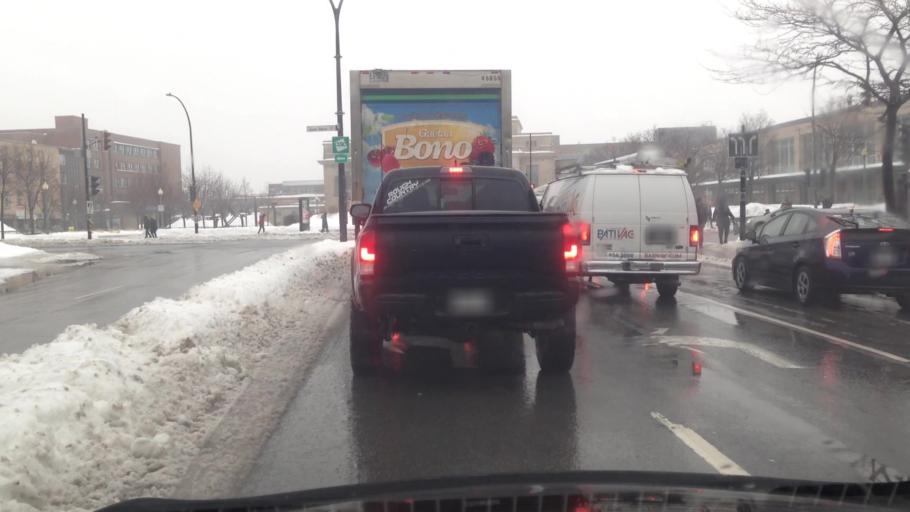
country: CA
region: Quebec
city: Mont-Royal
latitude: 45.5301
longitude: -73.6217
